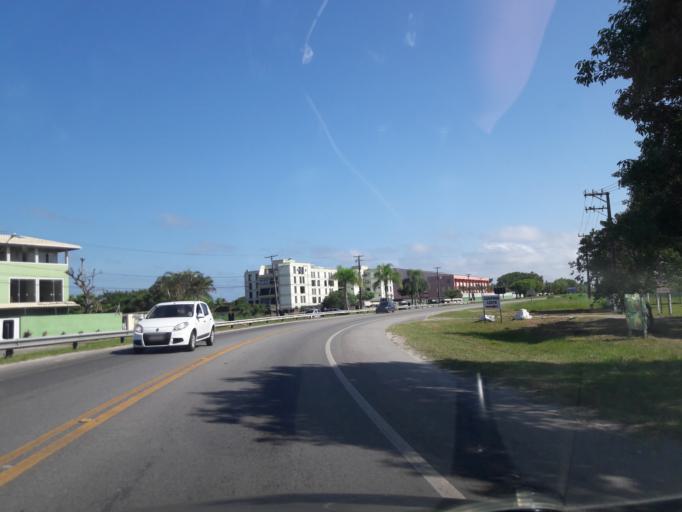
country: BR
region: Parana
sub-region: Pontal Do Parana
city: Pontal do Parana
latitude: -25.6997
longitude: -48.4733
